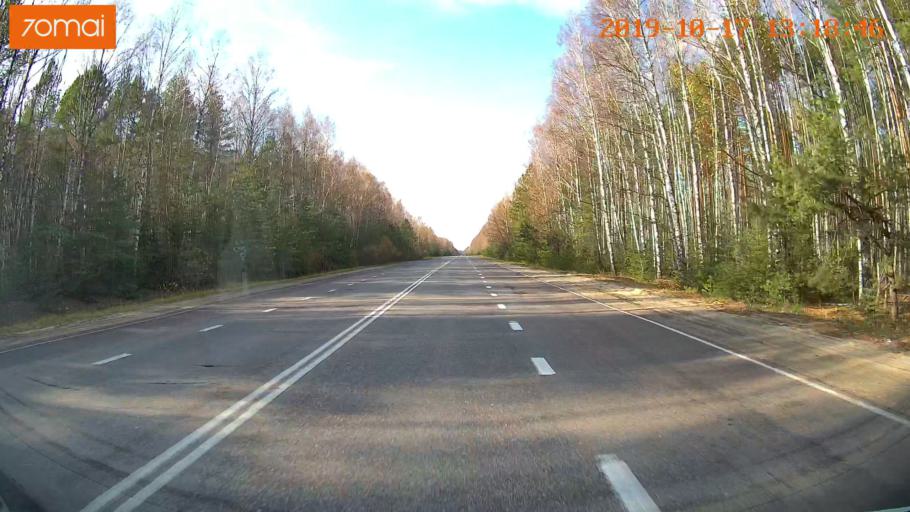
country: RU
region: Rjazan
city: Gus'-Zheleznyy
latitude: 55.0651
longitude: 41.0901
